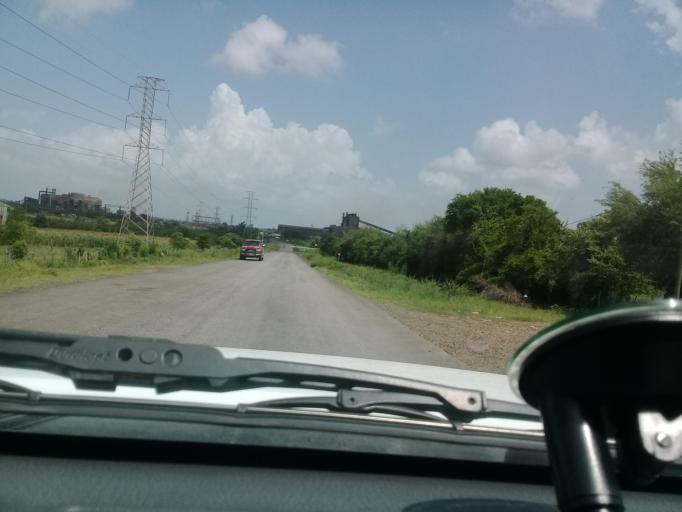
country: MX
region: Veracruz
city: Moralillo
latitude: 22.2291
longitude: -98.0162
